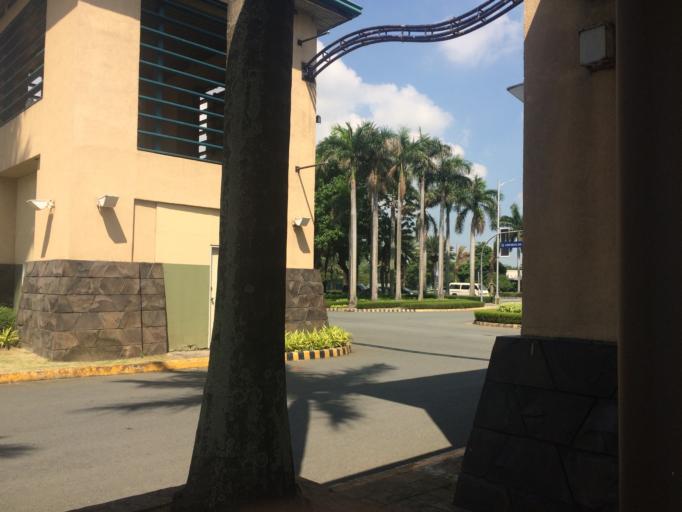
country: PH
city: Sambayanihan People's Village
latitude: 14.4181
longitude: 121.0391
